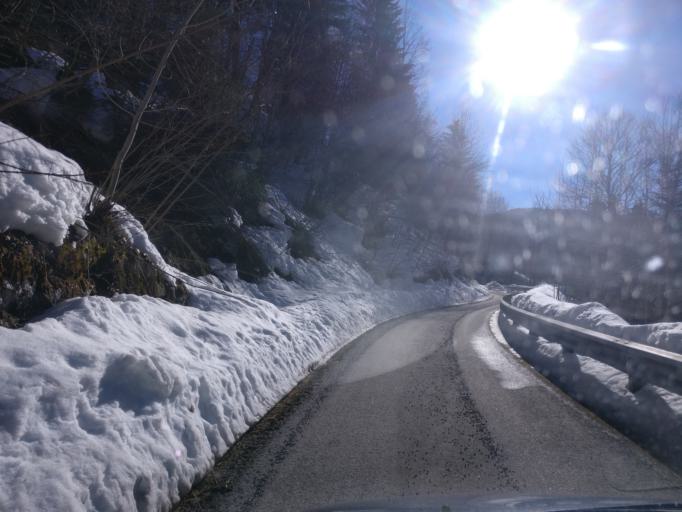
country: AT
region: Salzburg
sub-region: Politischer Bezirk Sankt Johann im Pongau
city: Wagrain
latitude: 47.3375
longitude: 13.2520
